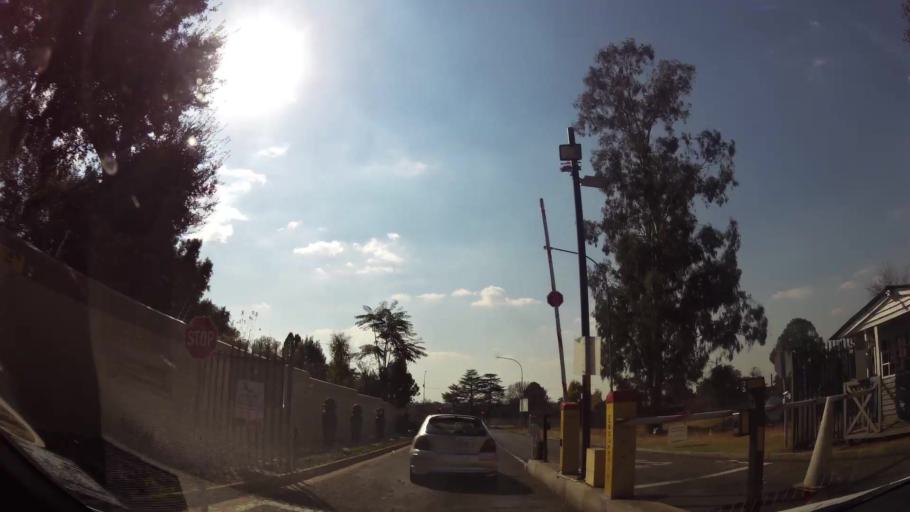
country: ZA
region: Gauteng
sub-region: Ekurhuleni Metropolitan Municipality
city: Benoni
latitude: -26.1822
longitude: 28.2932
